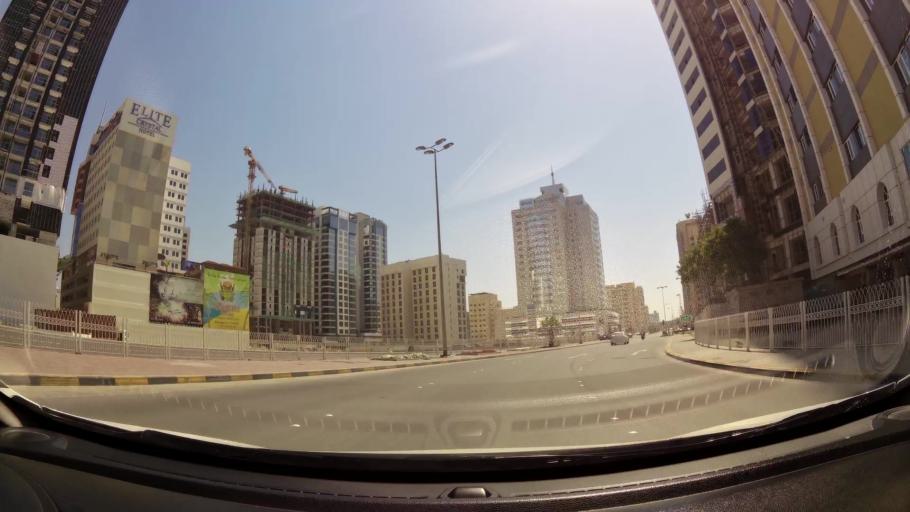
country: BH
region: Manama
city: Manama
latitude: 26.2162
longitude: 50.6098
